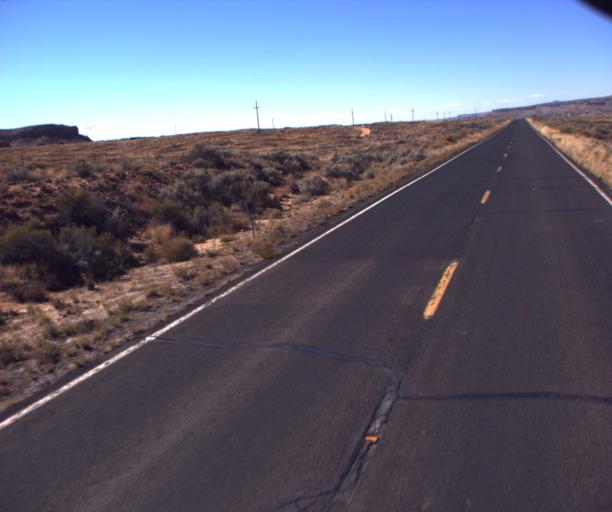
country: US
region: Arizona
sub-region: Navajo County
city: First Mesa
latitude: 35.8729
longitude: -110.5639
